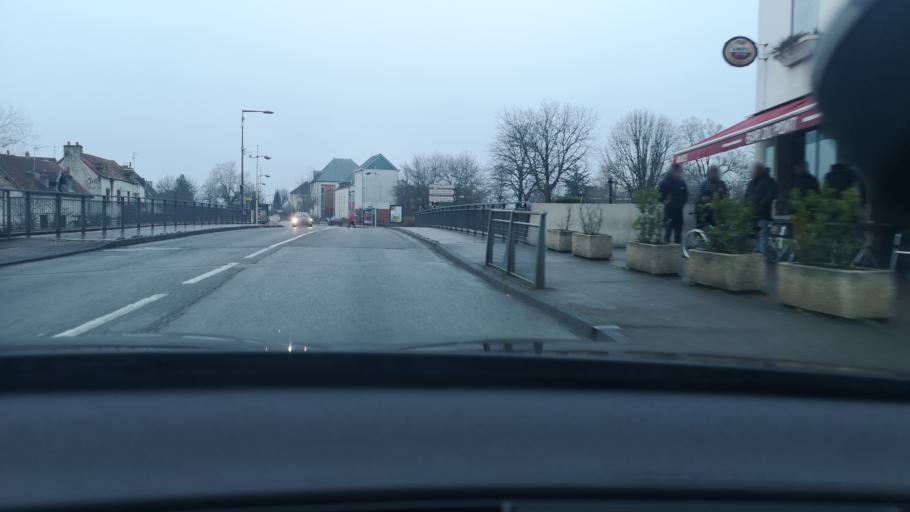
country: FR
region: Bourgogne
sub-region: Departement de la Cote-d'Or
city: Longvic
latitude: 47.2855
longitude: 5.0631
